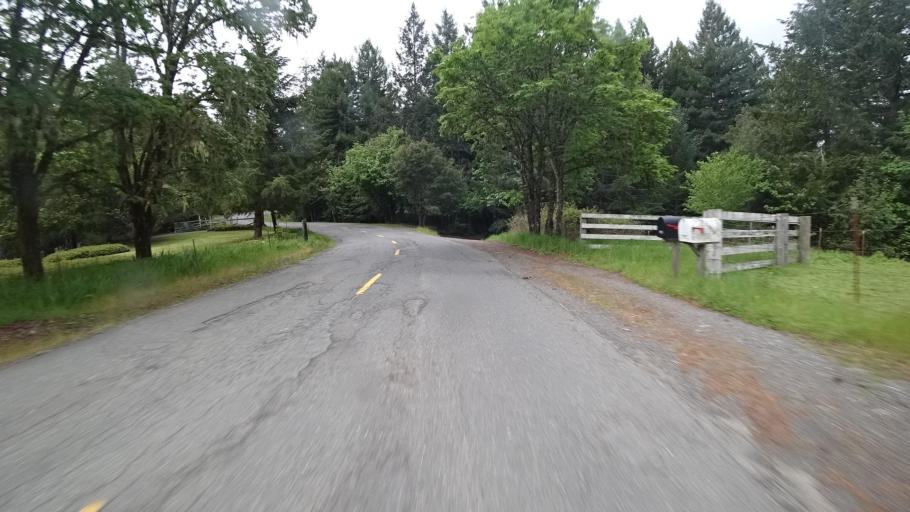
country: US
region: California
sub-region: Humboldt County
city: Redway
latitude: 40.2835
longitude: -123.7987
